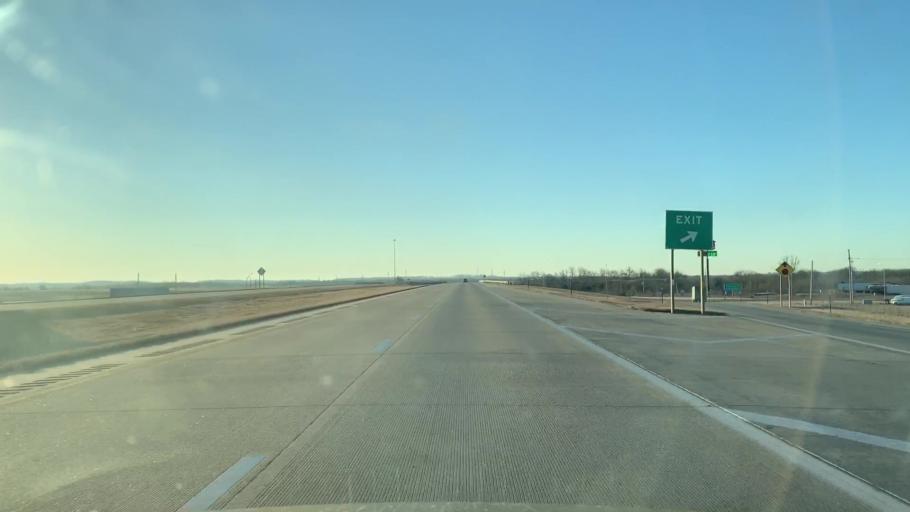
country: US
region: Kansas
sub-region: Linn County
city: Pleasanton
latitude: 38.1842
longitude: -94.7012
